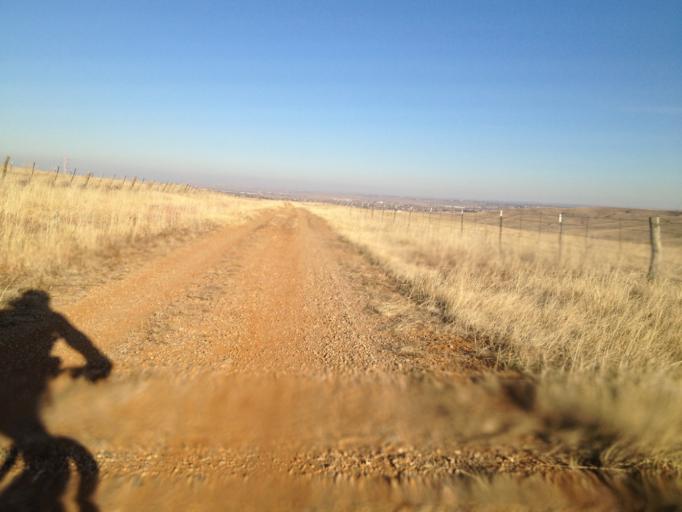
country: US
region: Colorado
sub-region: Boulder County
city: Superior
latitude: 39.9168
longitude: -105.2004
